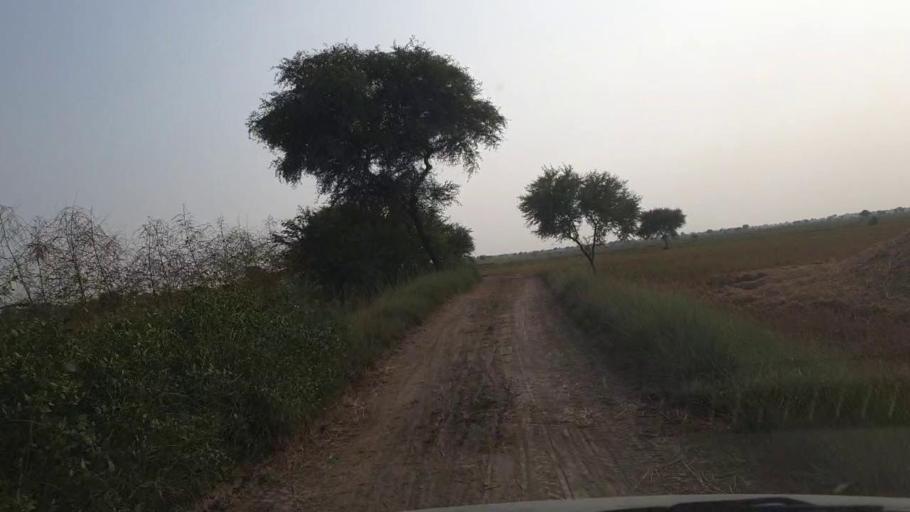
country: PK
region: Sindh
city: Matli
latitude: 25.0418
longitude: 68.7491
